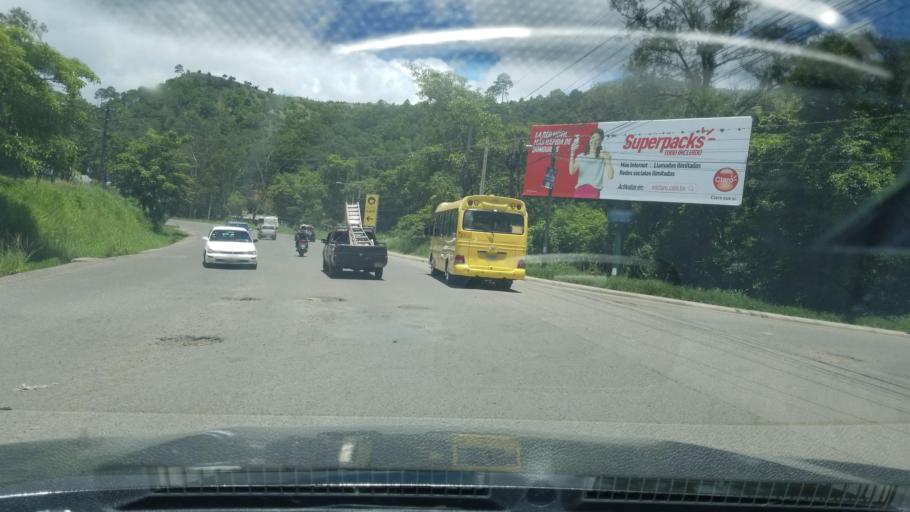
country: HN
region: Francisco Morazan
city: Rio Abajo
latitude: 14.1350
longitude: -87.2339
